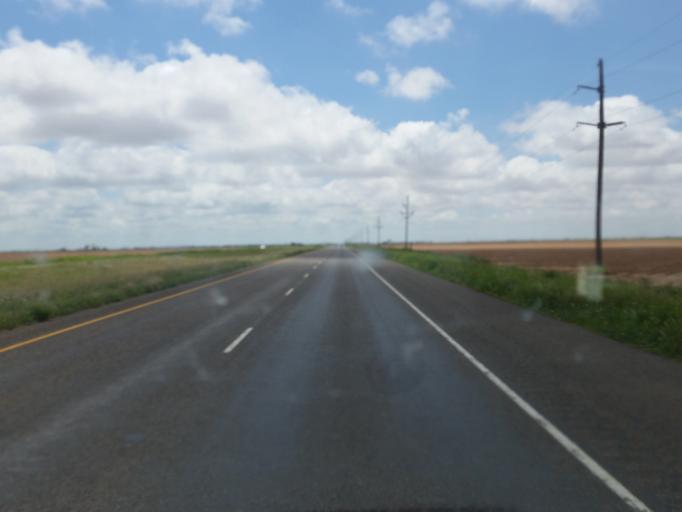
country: US
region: Texas
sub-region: Lubbock County
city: Slaton
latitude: 33.3863
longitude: -101.5936
